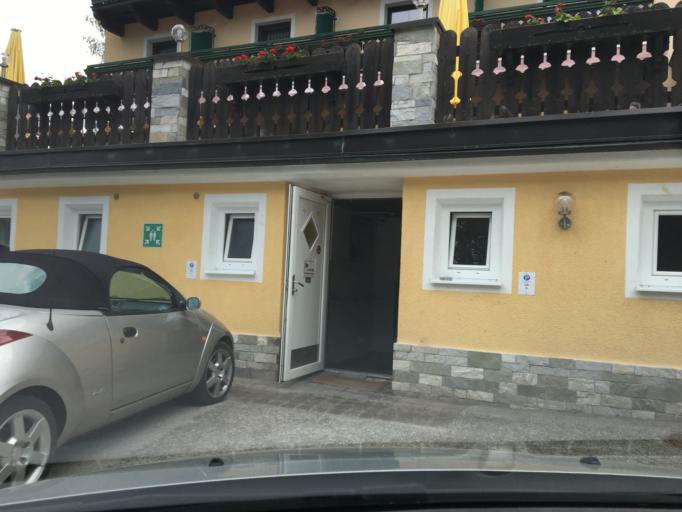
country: AT
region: Salzburg
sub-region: Politischer Bezirk Sankt Johann im Pongau
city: Wagrain
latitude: 47.3301
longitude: 13.3051
